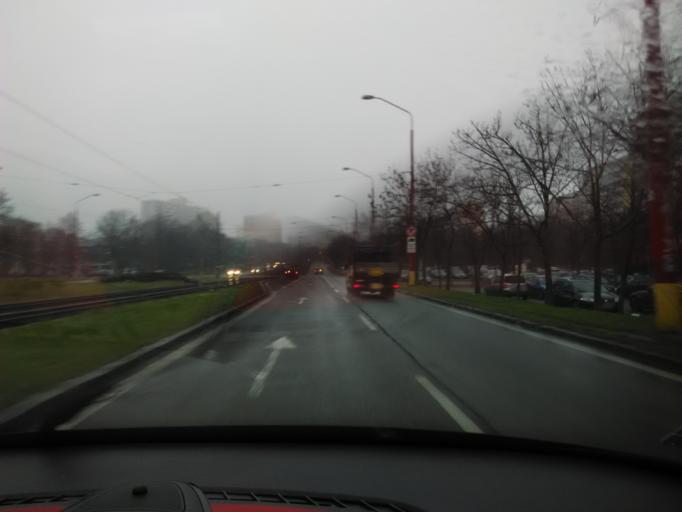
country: AT
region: Lower Austria
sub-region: Politischer Bezirk Bruck an der Leitha
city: Wolfsthal
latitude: 48.1802
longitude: 17.0430
